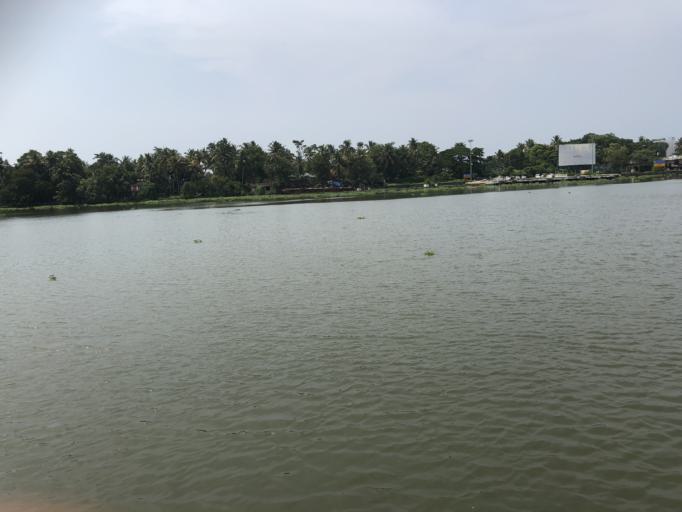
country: IN
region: Kerala
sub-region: Ernakulam
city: Cochin
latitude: 9.9903
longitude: 76.2686
